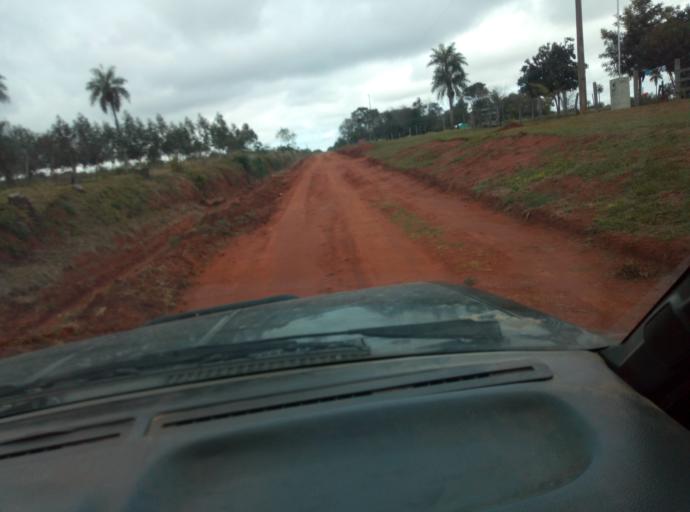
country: PY
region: Caaguazu
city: Doctor Cecilio Baez
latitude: -25.1470
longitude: -56.2904
